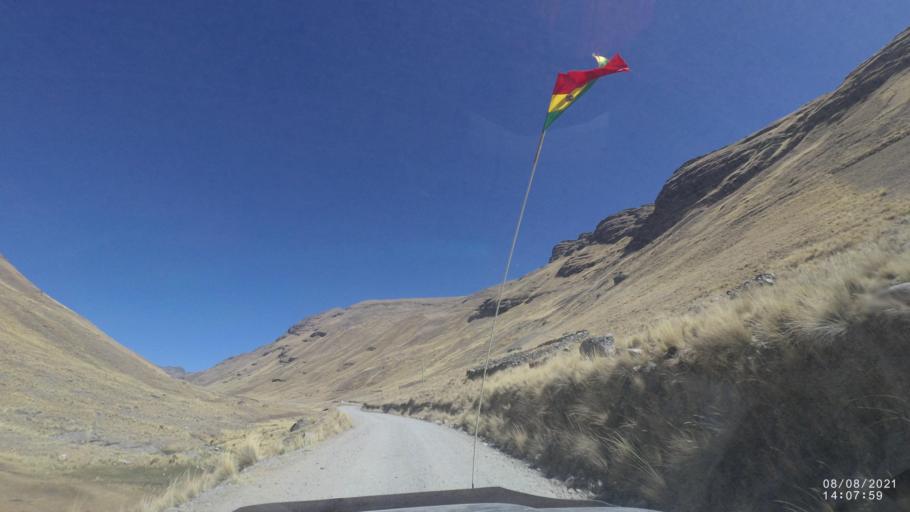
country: BO
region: Cochabamba
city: Sipe Sipe
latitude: -17.1341
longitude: -66.4399
